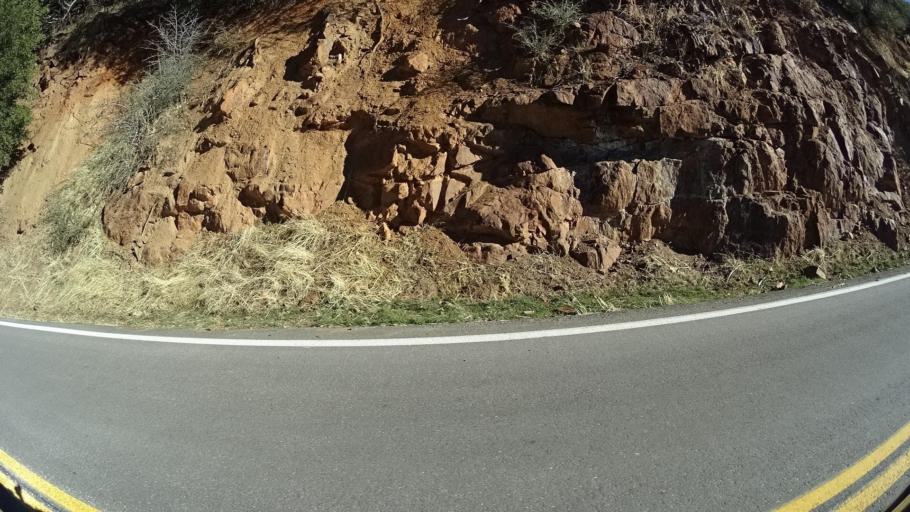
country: US
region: California
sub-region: Kern County
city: Alta Sierra
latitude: 35.7427
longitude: -118.5768
